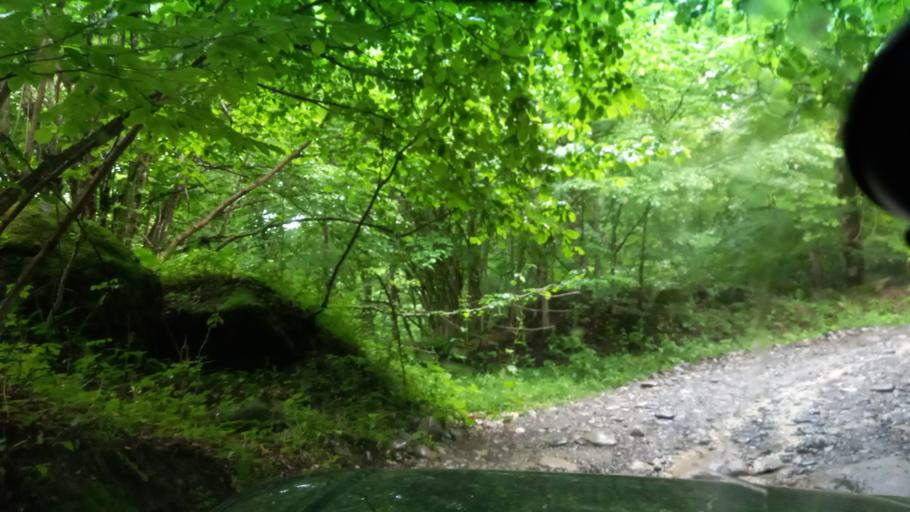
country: RU
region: Krasnodarskiy
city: Psebay
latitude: 44.0142
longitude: 40.7156
